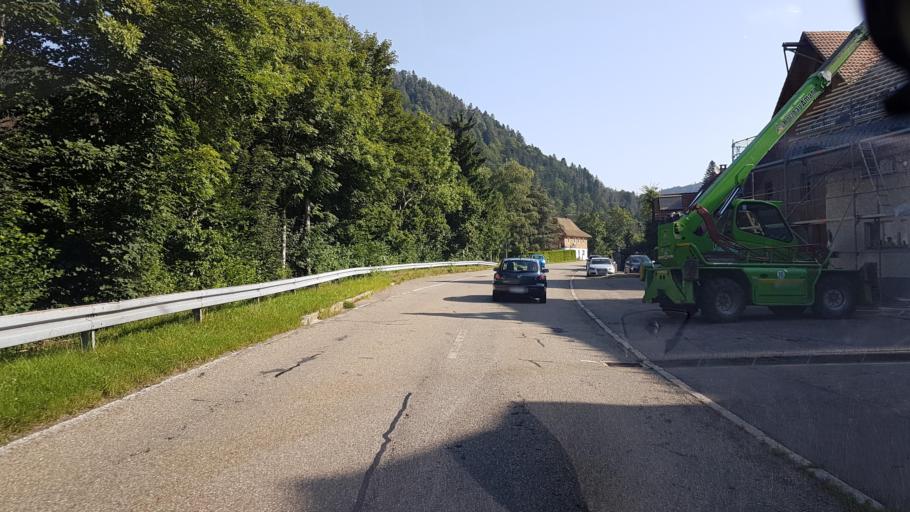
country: DE
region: Baden-Wuerttemberg
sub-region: Freiburg Region
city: Dachsberg
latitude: 47.7176
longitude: 8.1289
